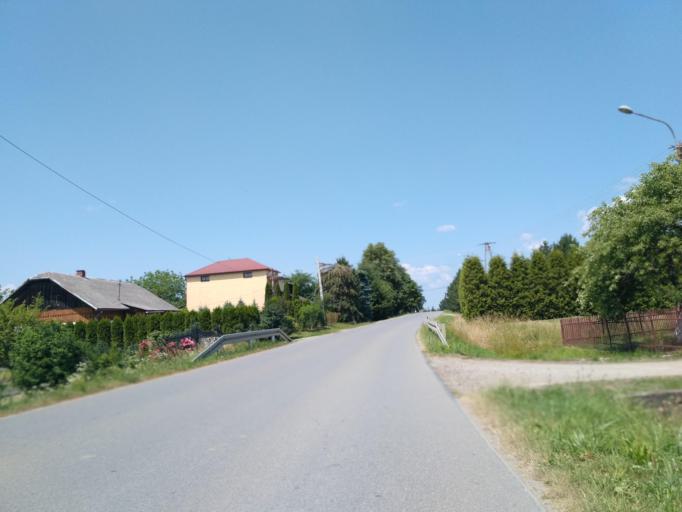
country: PL
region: Subcarpathian Voivodeship
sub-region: Powiat sanocki
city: Niebieszczany
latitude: 49.5164
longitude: 22.1381
